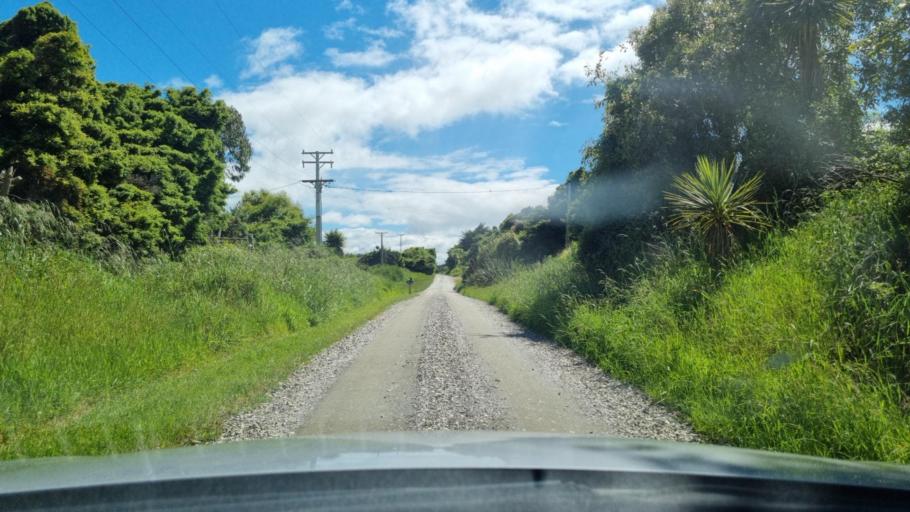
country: NZ
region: Southland
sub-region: Invercargill City
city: Invercargill
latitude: -46.4554
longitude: 168.2813
